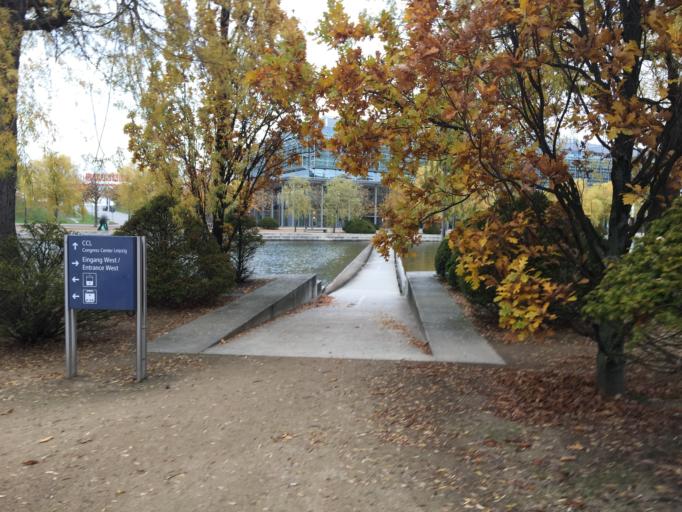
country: DE
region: Saxony
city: Rackwitz
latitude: 51.3967
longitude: 12.3977
